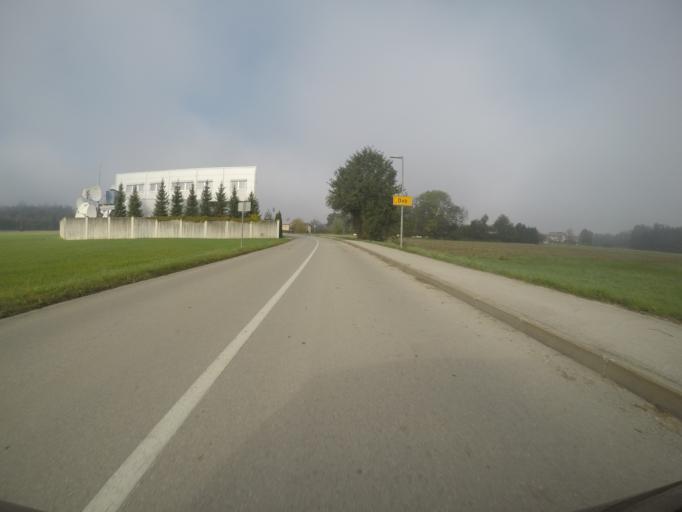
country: SI
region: Domzale
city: Dob
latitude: 46.1494
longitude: 14.6349
